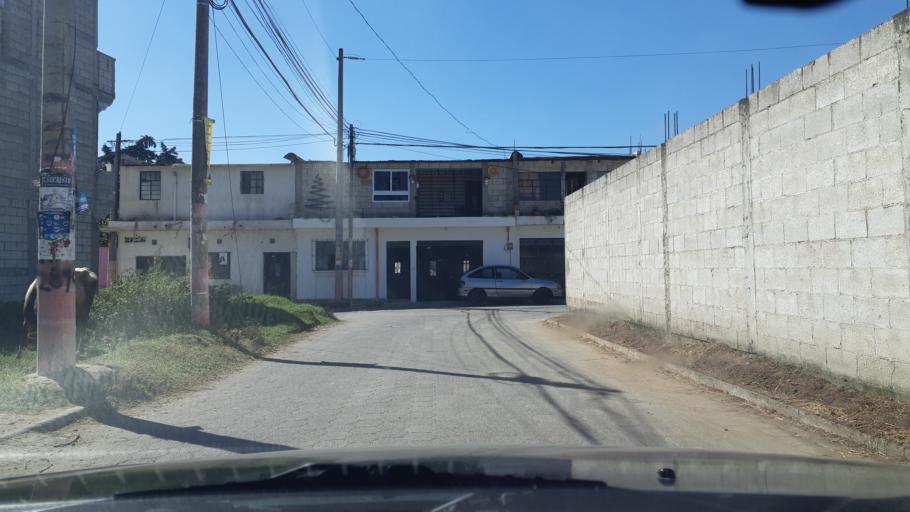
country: GT
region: Chimaltenango
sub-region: Municipio de Chimaltenango
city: Chimaltenango
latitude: 14.6603
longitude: -90.8049
